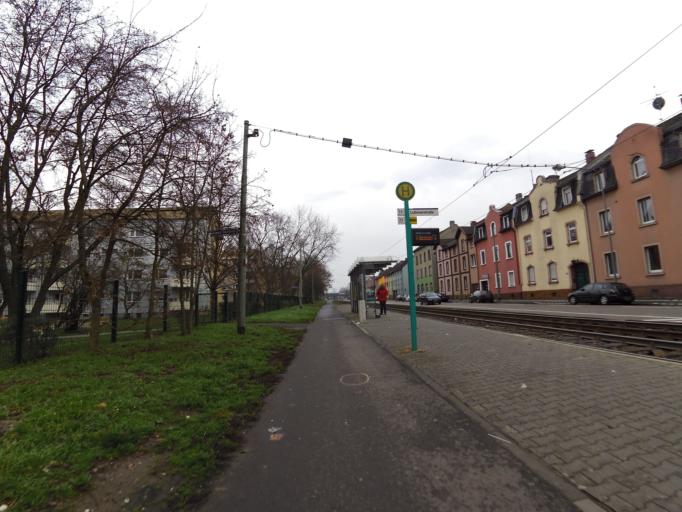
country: DE
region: Hesse
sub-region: Regierungsbezirk Darmstadt
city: Eschborn
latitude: 50.0994
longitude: 8.5733
